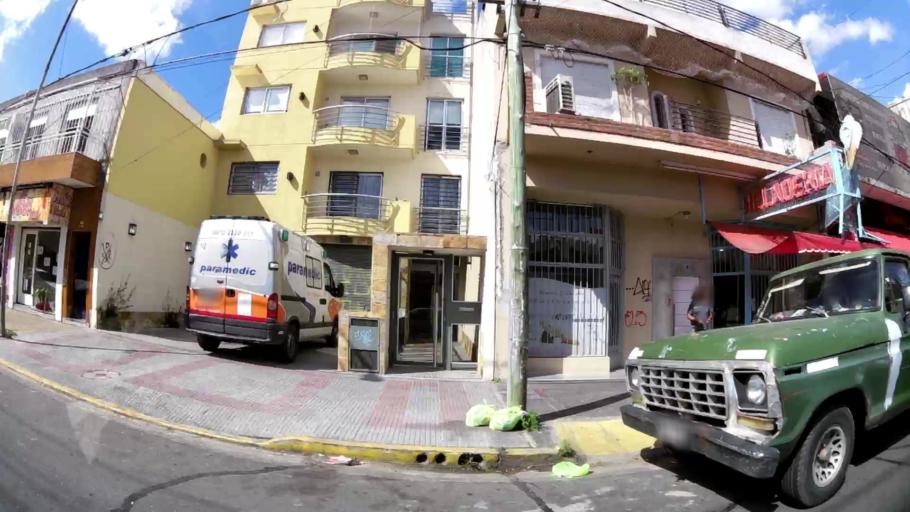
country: AR
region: Buenos Aires
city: San Justo
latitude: -34.6476
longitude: -58.5574
